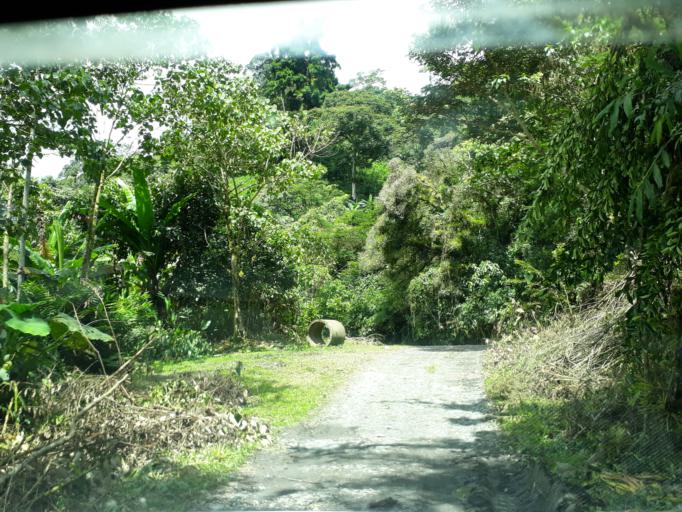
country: CO
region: Cundinamarca
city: Topaipi
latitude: 5.3138
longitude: -74.2126
